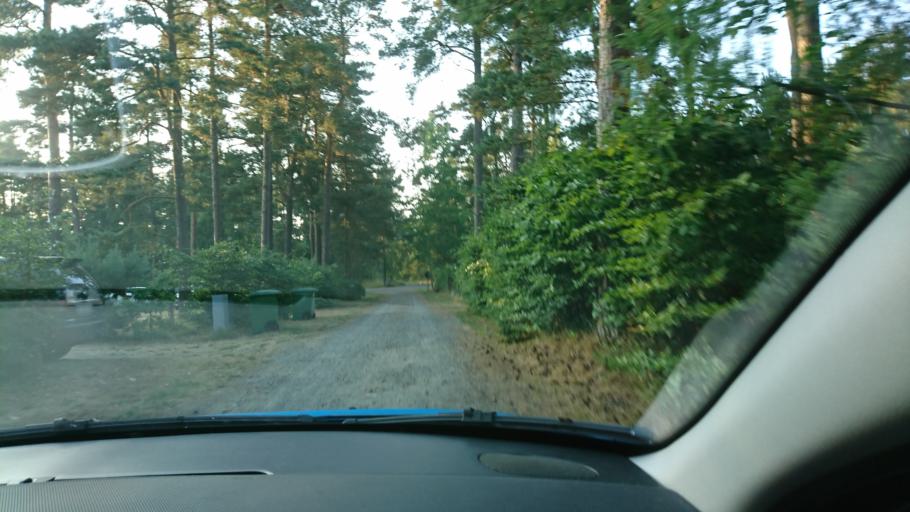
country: SE
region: Skane
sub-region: Simrishamns Kommun
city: Kivik
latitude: 55.7122
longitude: 14.1725
